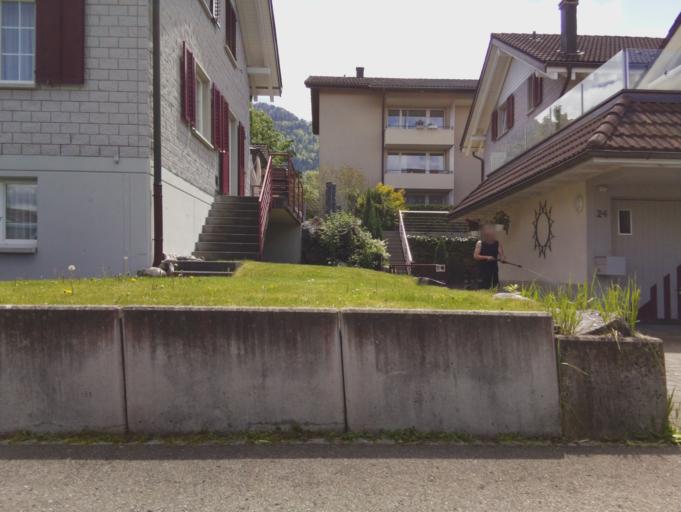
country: CH
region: Schwyz
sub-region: Bezirk March
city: Schubelbach
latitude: 47.1782
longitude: 8.9034
